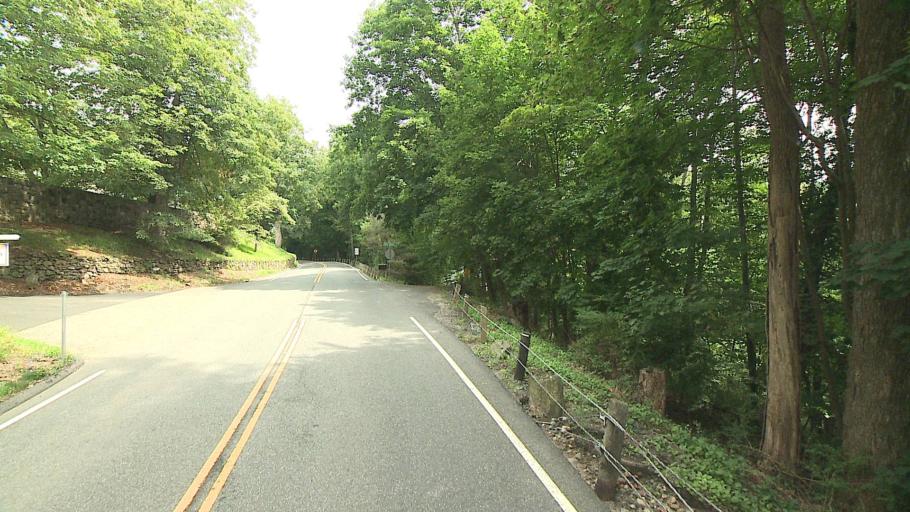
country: US
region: Connecticut
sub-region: Litchfield County
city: New Preston
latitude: 41.6260
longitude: -73.3104
